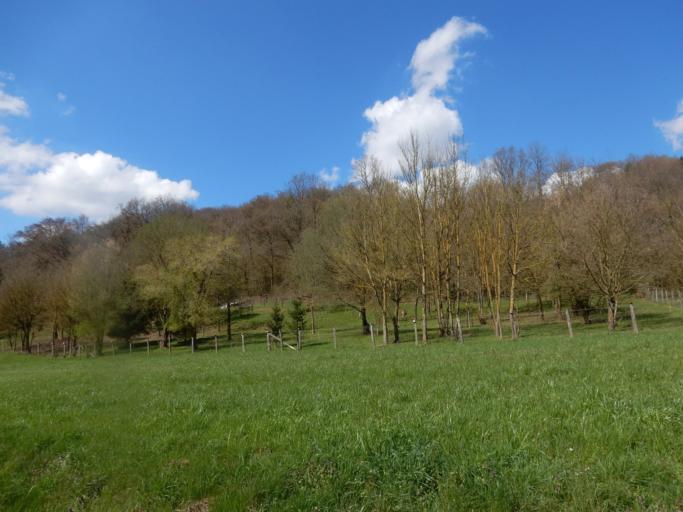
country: DE
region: Rheinland-Pfalz
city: Wallendorf
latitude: 49.8719
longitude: 6.2815
